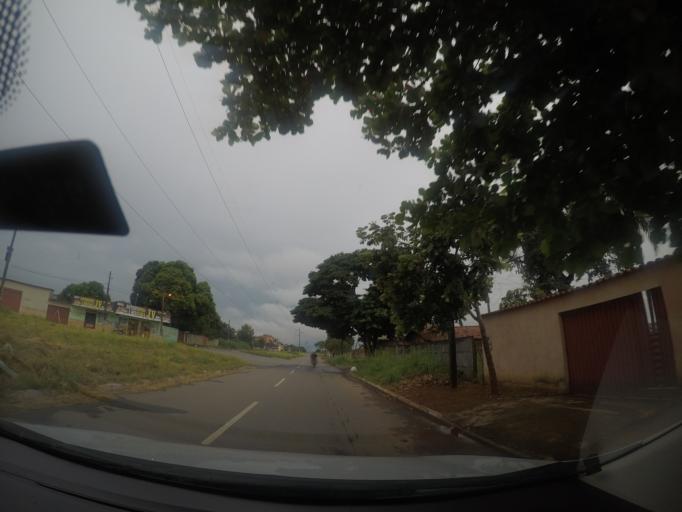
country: BR
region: Goias
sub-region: Aparecida De Goiania
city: Aparecida de Goiania
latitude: -16.7578
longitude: -49.3115
